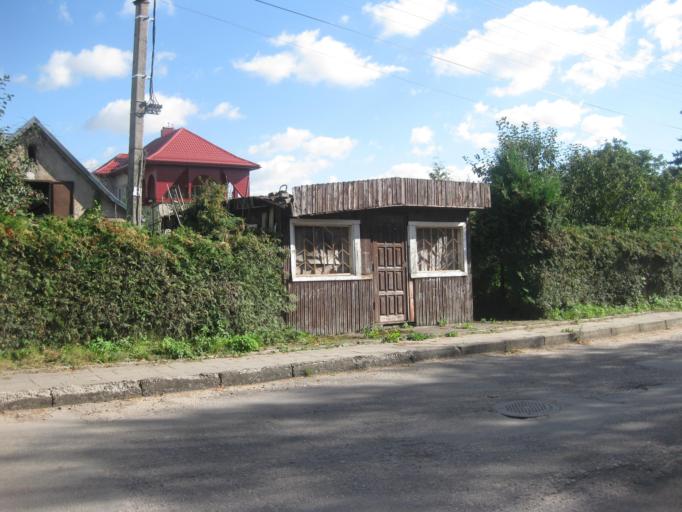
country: LT
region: Kauno apskritis
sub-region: Kauno rajonas
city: Garliava
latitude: 54.8332
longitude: 23.8710
